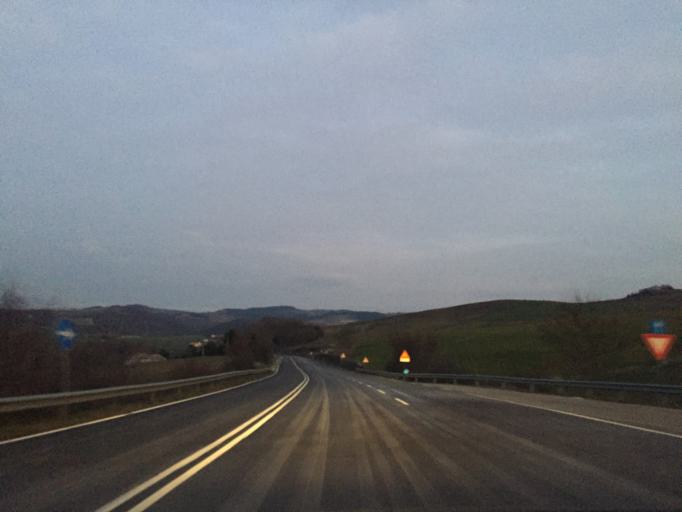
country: IT
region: Apulia
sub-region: Provincia di Foggia
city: Volturara Appula
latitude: 41.4570
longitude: 15.0640
